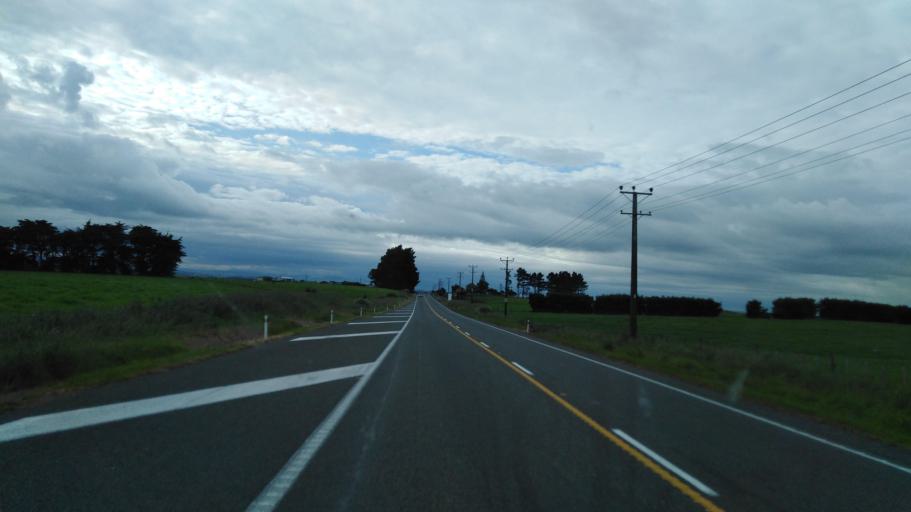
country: NZ
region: Manawatu-Wanganui
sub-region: Rangitikei District
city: Bulls
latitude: -40.1370
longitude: 175.3647
